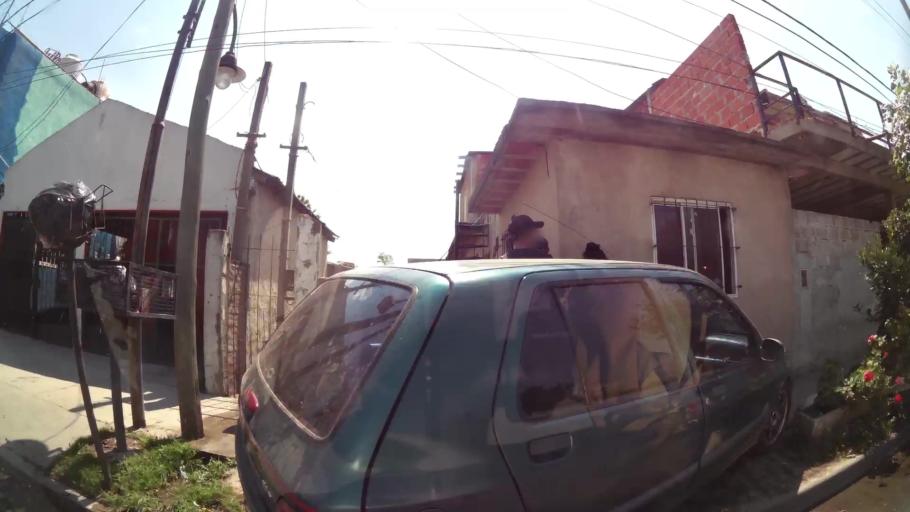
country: AR
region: Buenos Aires
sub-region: Partido de Tigre
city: Tigre
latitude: -34.4717
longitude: -58.5971
